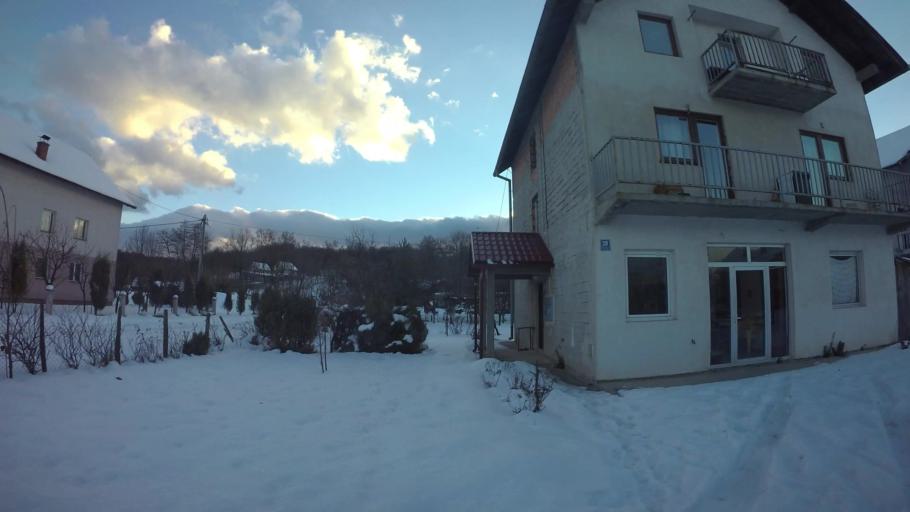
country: BA
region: Federation of Bosnia and Herzegovina
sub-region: Kanton Sarajevo
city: Sarajevo
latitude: 43.8086
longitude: 18.3652
